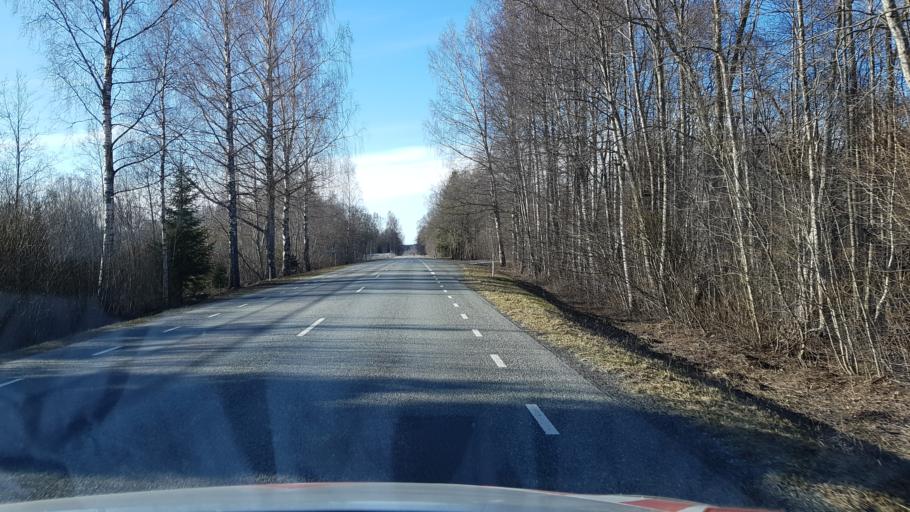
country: EE
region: Laeaene-Virumaa
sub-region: Tapa vald
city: Tapa
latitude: 59.4388
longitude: 25.9592
